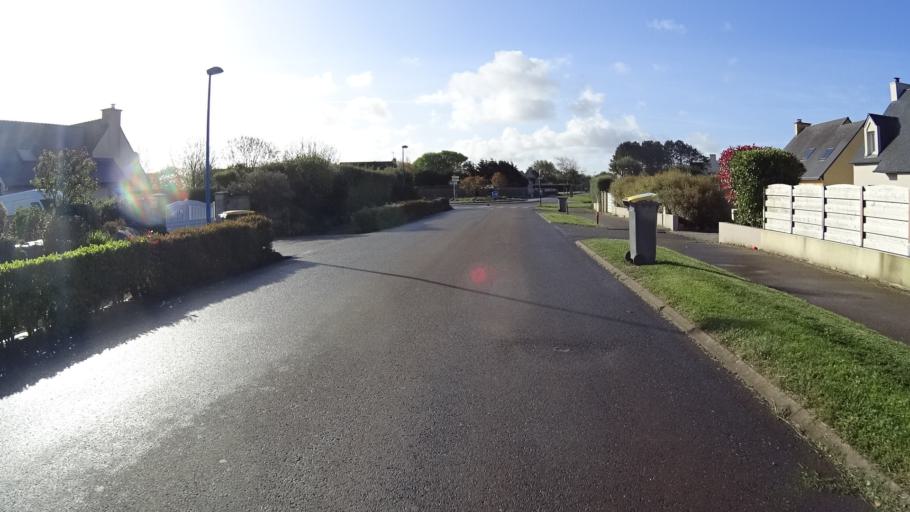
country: FR
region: Brittany
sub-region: Departement du Finistere
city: Plouarzel
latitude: 48.4313
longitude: -4.7348
